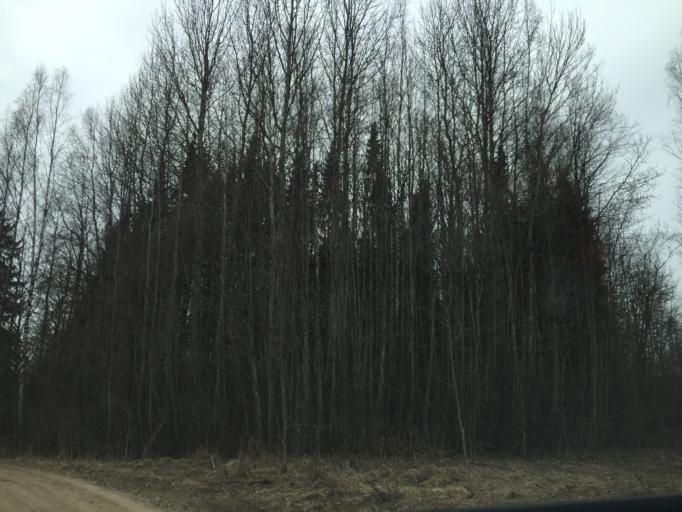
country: LV
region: Kraslavas Rajons
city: Kraslava
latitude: 55.9798
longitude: 27.1631
